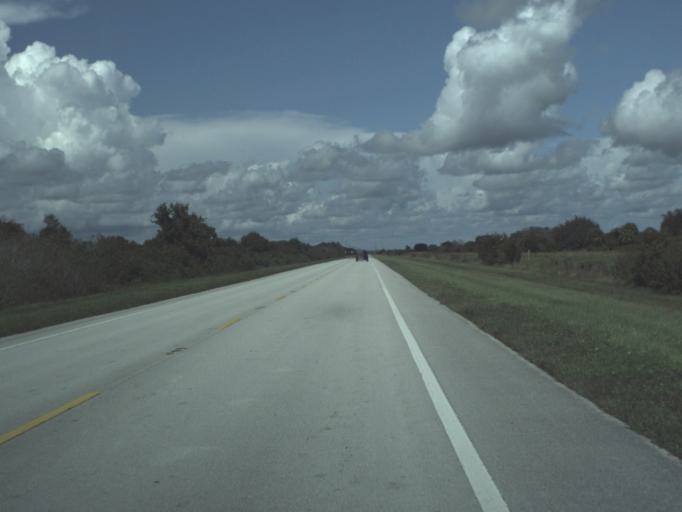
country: US
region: Florida
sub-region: Highlands County
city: Lake Placid
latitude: 27.4186
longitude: -81.2010
